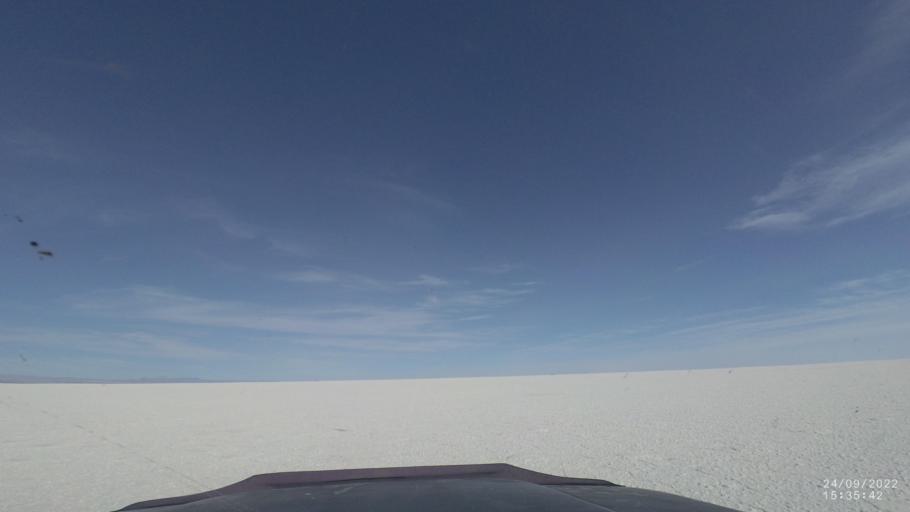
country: BO
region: Potosi
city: Colchani
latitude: -20.1382
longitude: -67.2520
